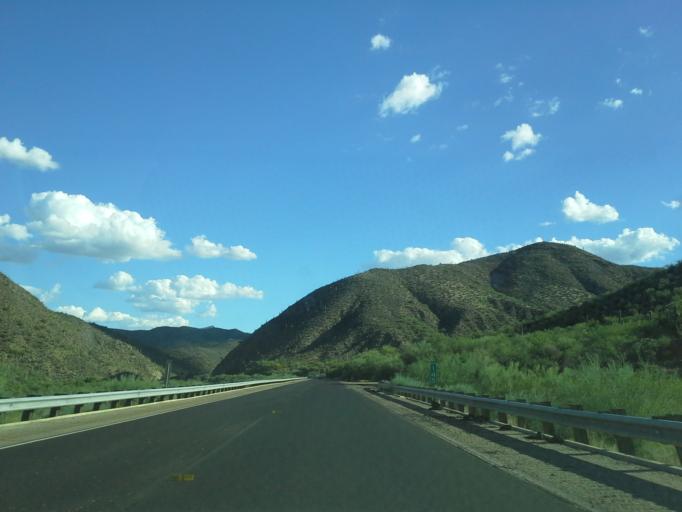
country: US
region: Arizona
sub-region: Pinal County
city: Kearny
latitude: 33.0643
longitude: -110.7248
